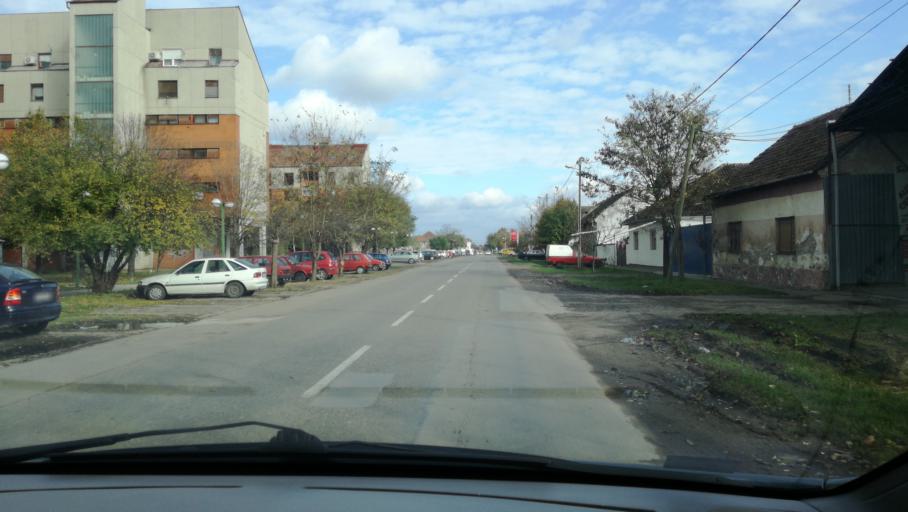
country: RS
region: Autonomna Pokrajina Vojvodina
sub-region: Severnobanatski Okrug
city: Kikinda
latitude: 45.8192
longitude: 20.4542
